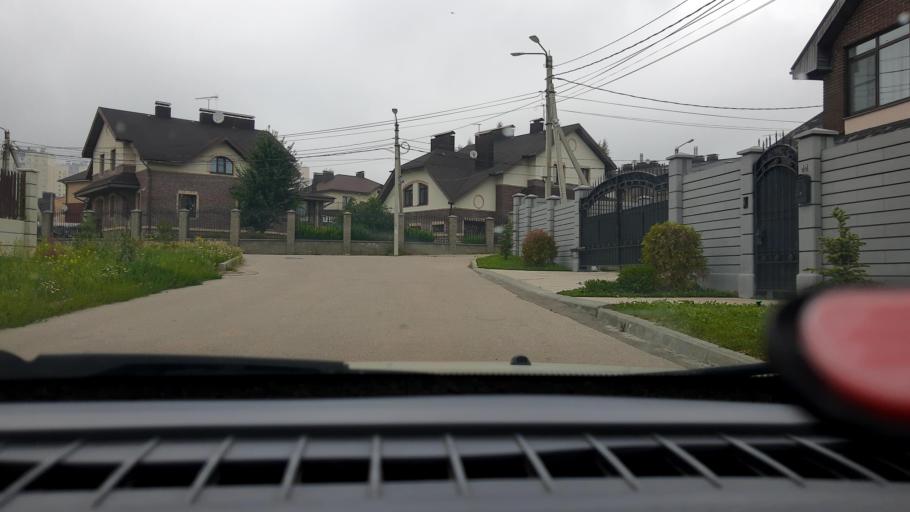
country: RU
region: Nizjnij Novgorod
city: Afonino
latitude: 56.2796
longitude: 44.0712
